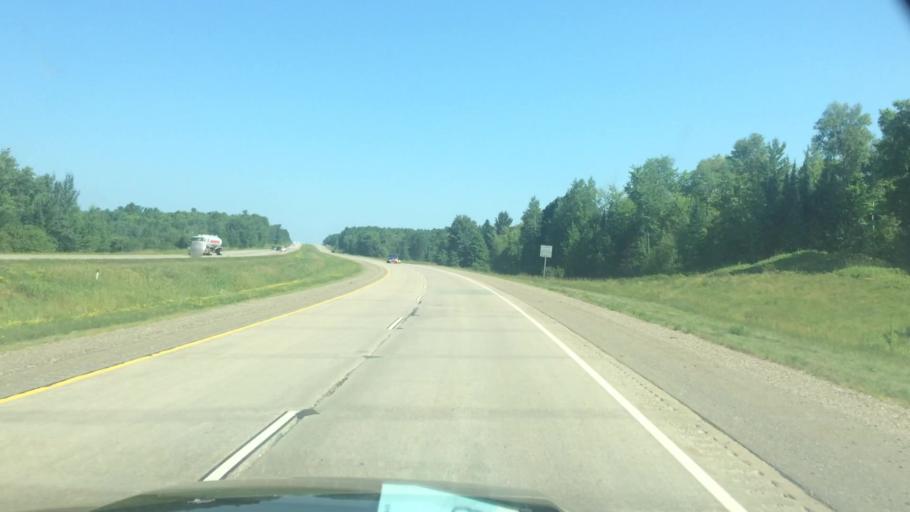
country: US
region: Wisconsin
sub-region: Lincoln County
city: Tomahawk
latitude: 45.3393
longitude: -89.6646
